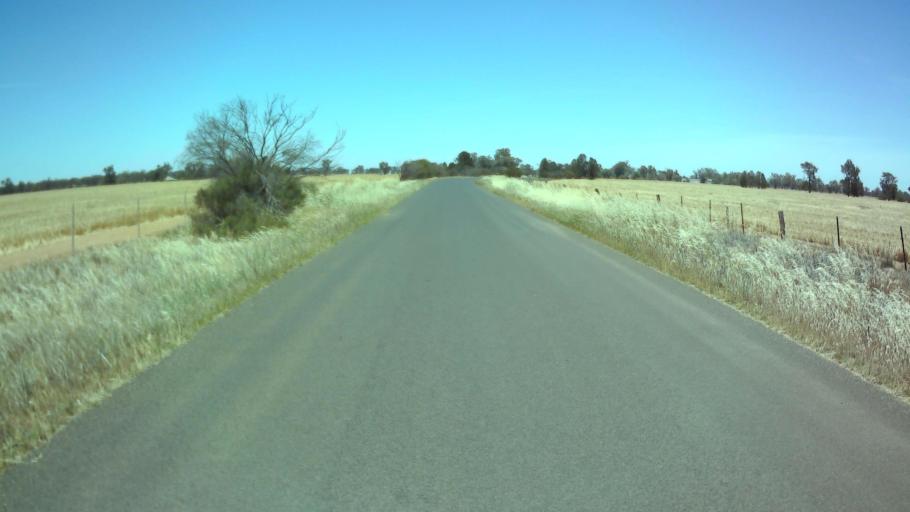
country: AU
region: New South Wales
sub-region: Weddin
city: Grenfell
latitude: -34.0545
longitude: 147.7810
